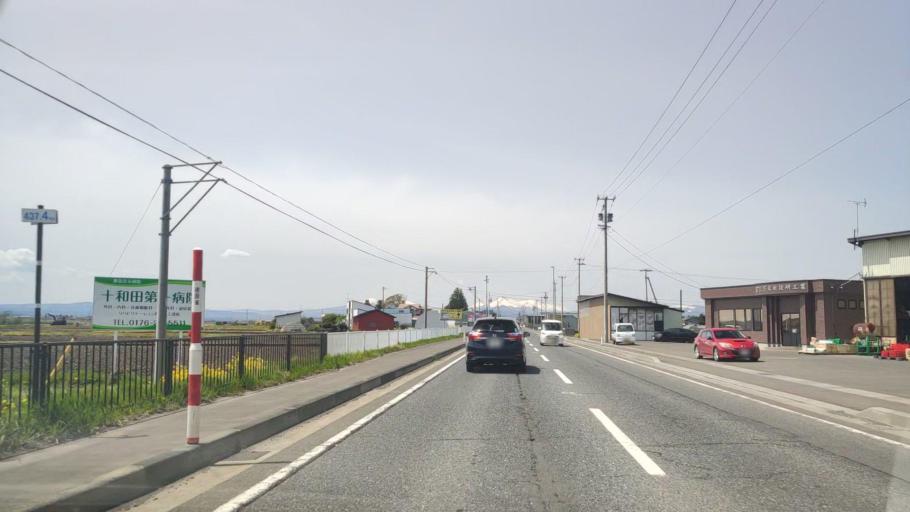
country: JP
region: Aomori
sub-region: Misawa Shi
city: Inuotose
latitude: 40.6099
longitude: 141.2797
